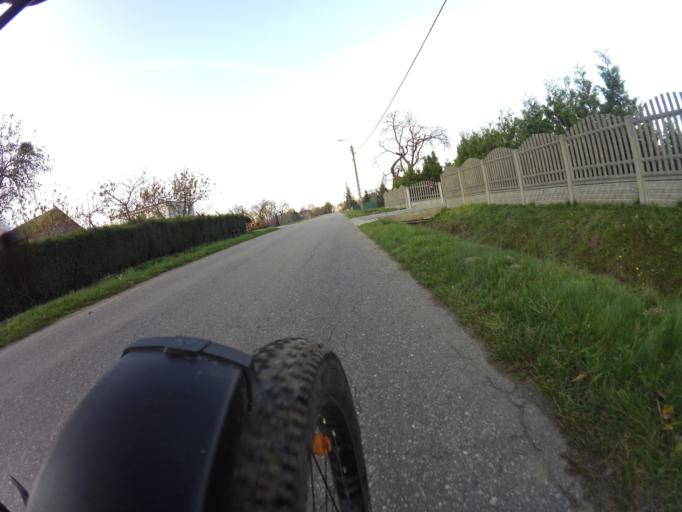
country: PL
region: Pomeranian Voivodeship
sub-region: Powiat pucki
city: Krokowa
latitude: 54.7578
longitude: 18.1838
